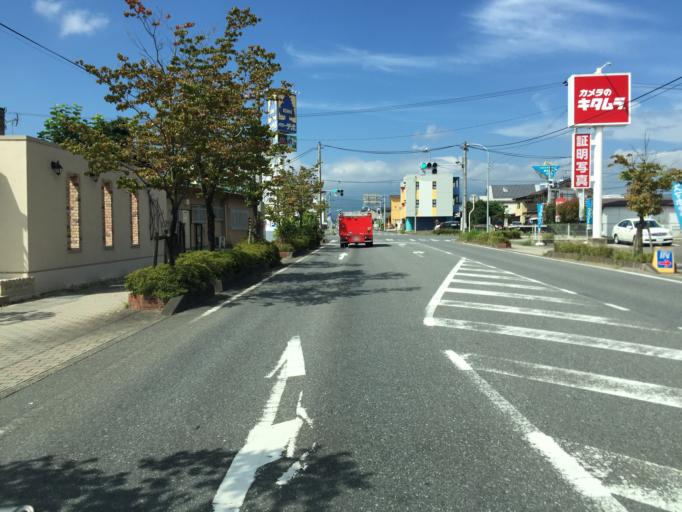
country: JP
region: Fukushima
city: Fukushima-shi
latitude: 37.7506
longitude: 140.4469
